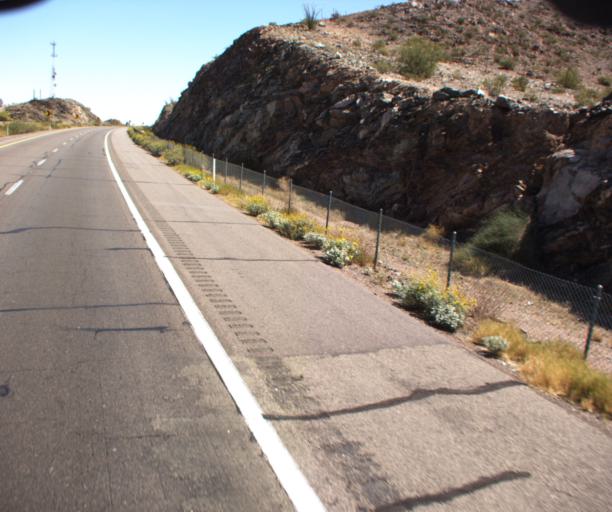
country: US
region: Arizona
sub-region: Yuma County
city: Wellton
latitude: 32.7254
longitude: -113.7518
